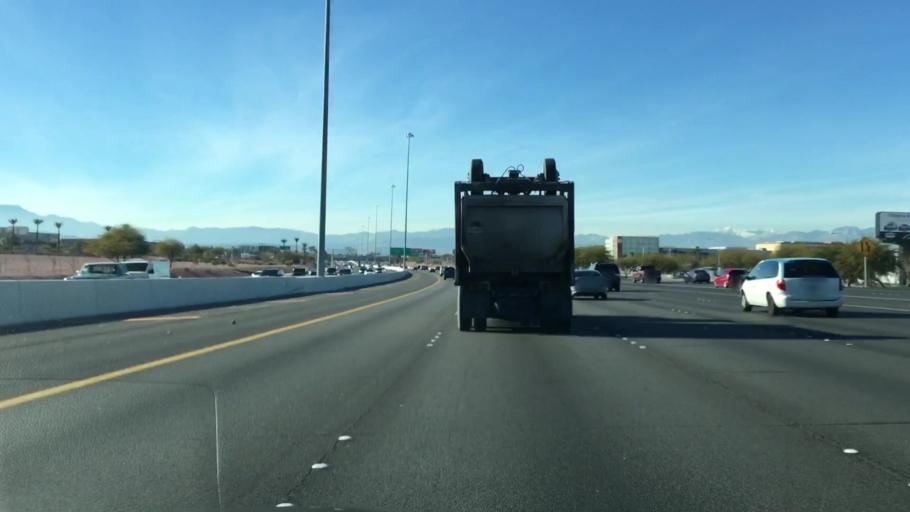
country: US
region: Nevada
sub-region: Clark County
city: Paradise
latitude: 36.0640
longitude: -115.1530
